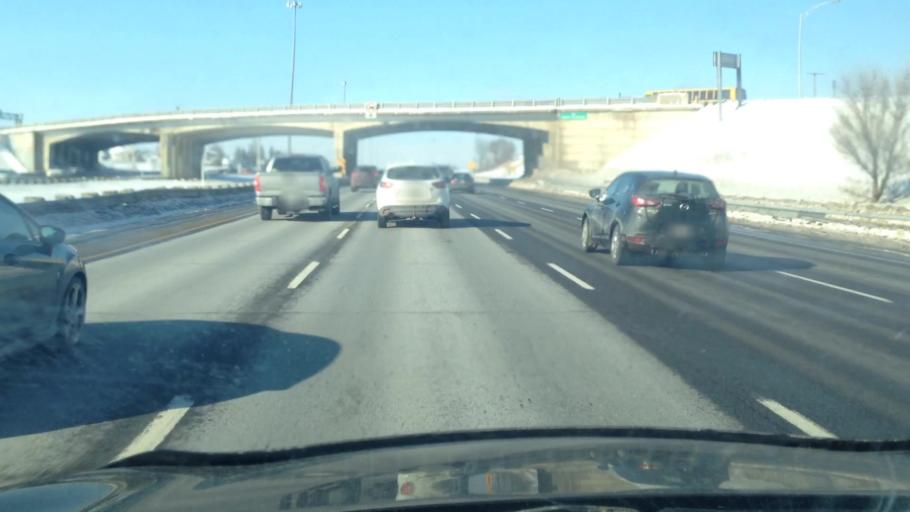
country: CA
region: Quebec
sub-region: Laurentides
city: Blainville
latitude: 45.6444
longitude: -73.8650
